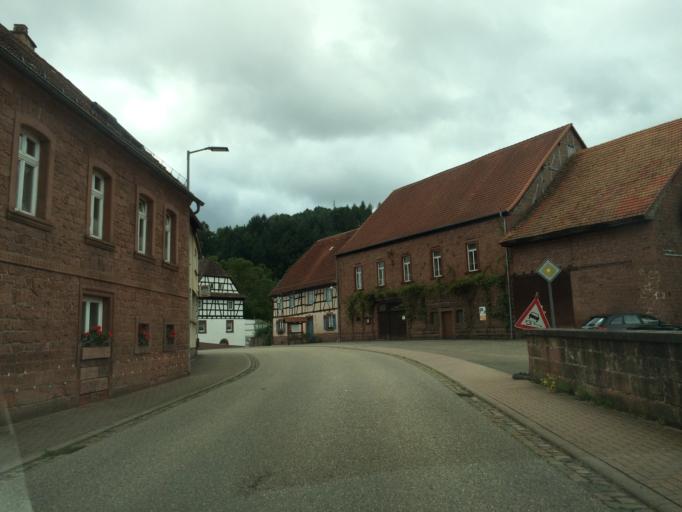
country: DE
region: Rheinland-Pfalz
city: Bundenthal
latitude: 49.0969
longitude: 7.8067
